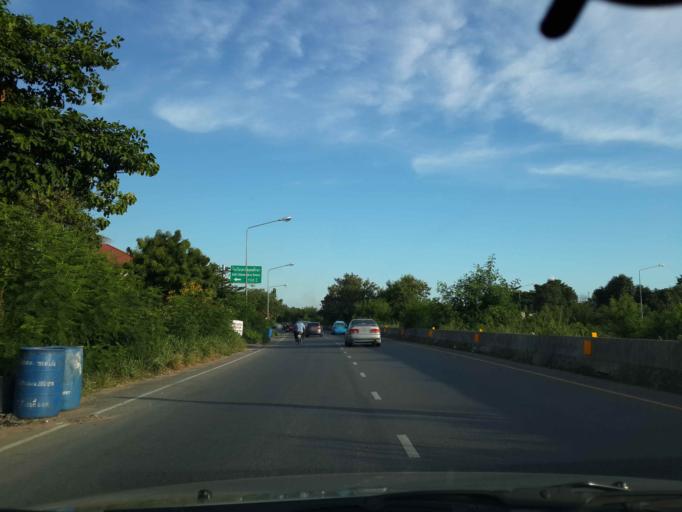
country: TH
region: Chon Buri
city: Phatthaya
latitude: 12.8936
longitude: 100.9002
